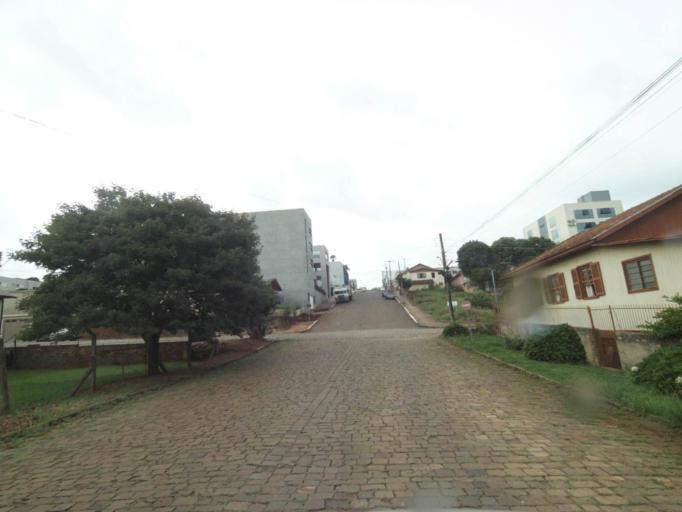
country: BR
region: Rio Grande do Sul
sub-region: Lagoa Vermelha
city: Lagoa Vermelha
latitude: -28.2069
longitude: -51.5271
